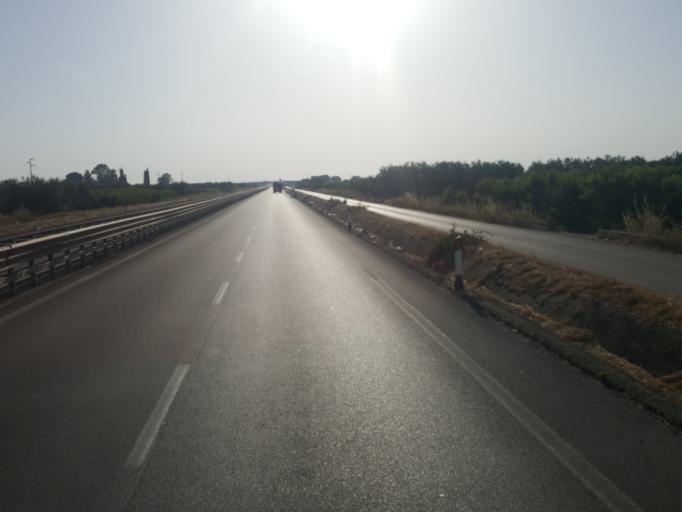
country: IT
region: Apulia
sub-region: Provincia di Barletta - Andria - Trani
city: San Ferdinando di Puglia
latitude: 41.3146
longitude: 16.1106
